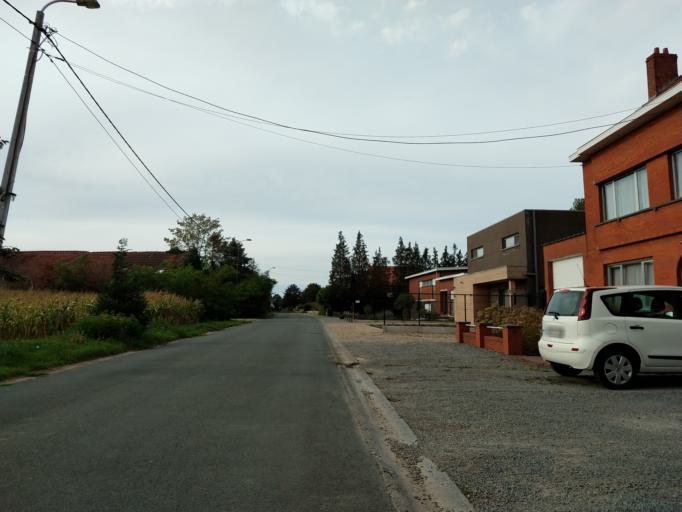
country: BE
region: Flanders
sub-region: Provincie Vlaams-Brabant
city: Haacht
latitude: 50.9804
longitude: 4.6492
